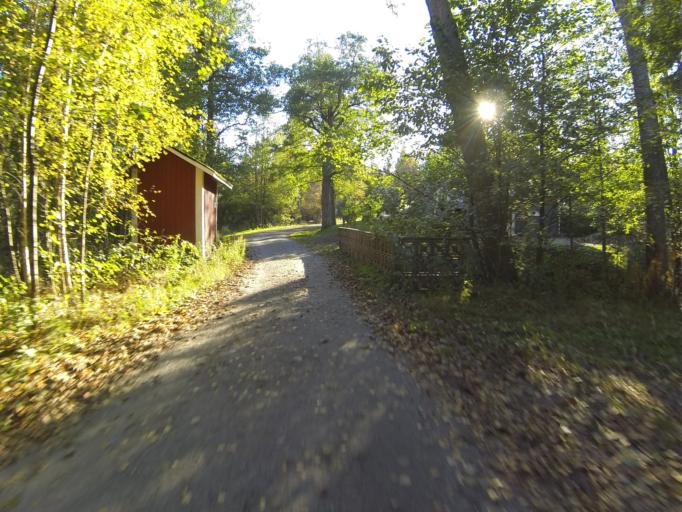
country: FI
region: Varsinais-Suomi
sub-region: Salo
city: Saerkisalo
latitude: 60.2151
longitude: 22.9182
